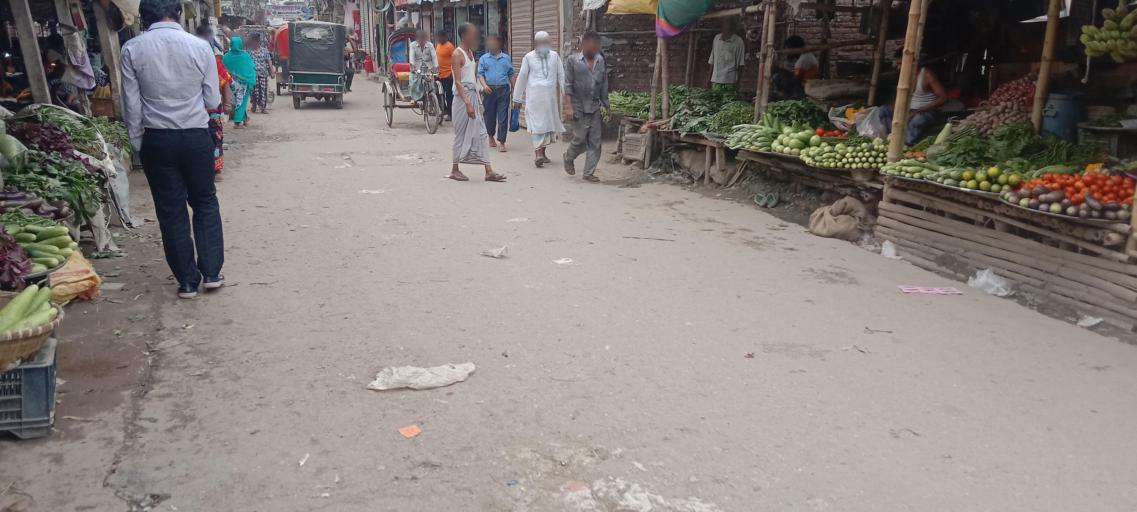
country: BD
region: Dhaka
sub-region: Dhaka
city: Dhaka
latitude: 23.6975
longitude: 90.3955
